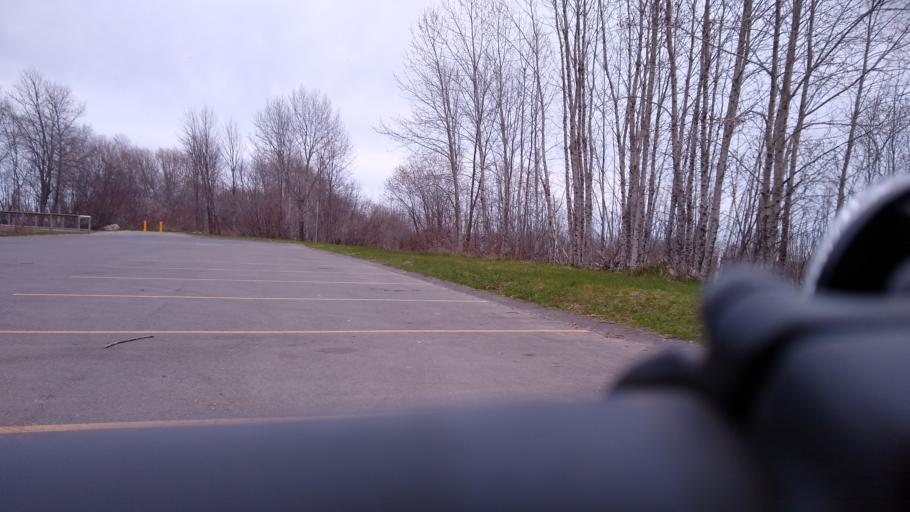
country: US
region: Michigan
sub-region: Delta County
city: Escanaba
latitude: 45.7065
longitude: -87.0799
